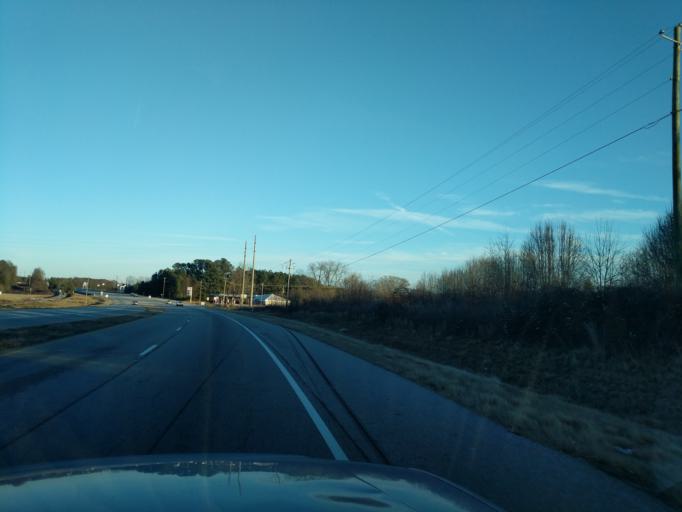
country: US
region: Georgia
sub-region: Franklin County
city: Lavonia
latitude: 34.4478
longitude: -83.1417
